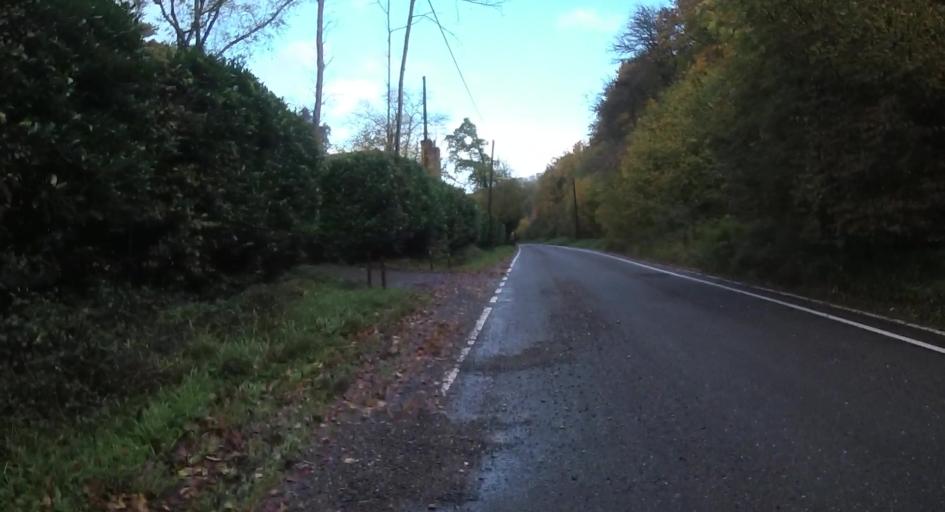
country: GB
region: England
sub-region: Hampshire
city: Alton
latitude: 51.1409
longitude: -1.0168
